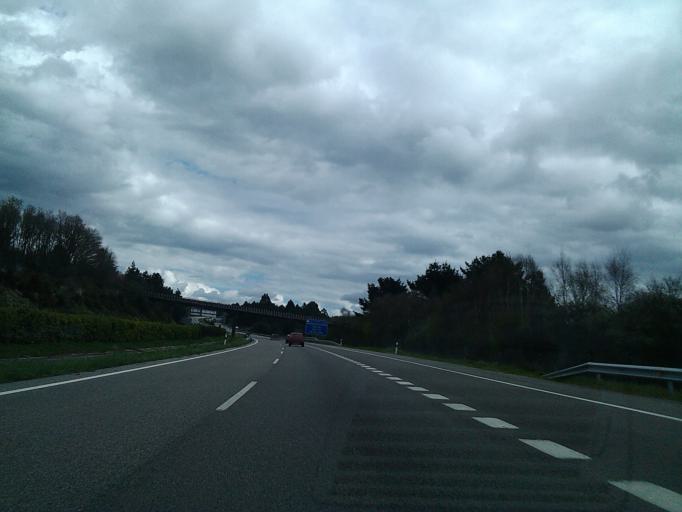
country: ES
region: Galicia
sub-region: Provincia de Lugo
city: Guitiriz
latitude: 43.1903
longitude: -7.8905
